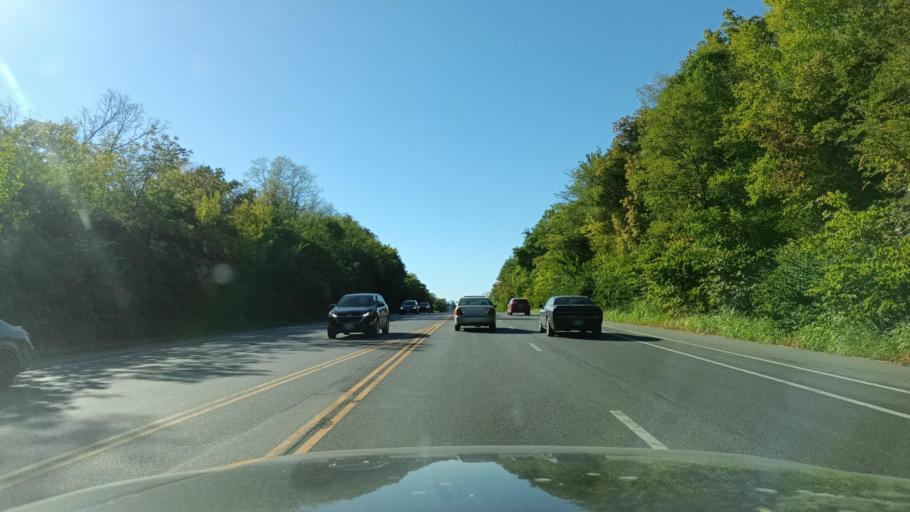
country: US
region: Missouri
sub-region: Boone County
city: Columbia
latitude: 38.9333
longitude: -92.3164
